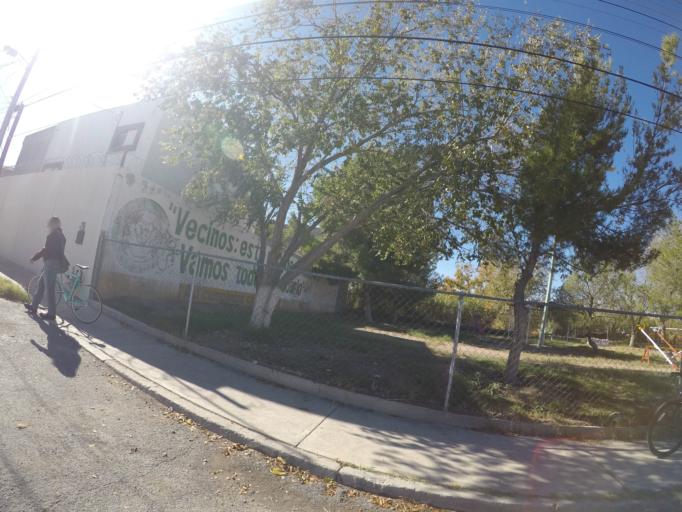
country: MX
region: Chihuahua
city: Ciudad Juarez
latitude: 31.7322
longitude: -106.4346
